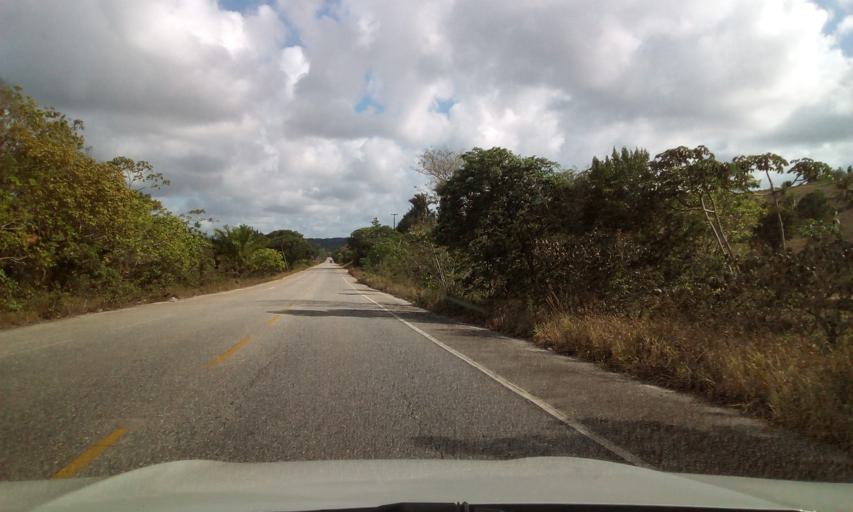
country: BR
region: Sergipe
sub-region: Indiaroba
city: Indiaroba
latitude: -11.4209
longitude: -37.4929
